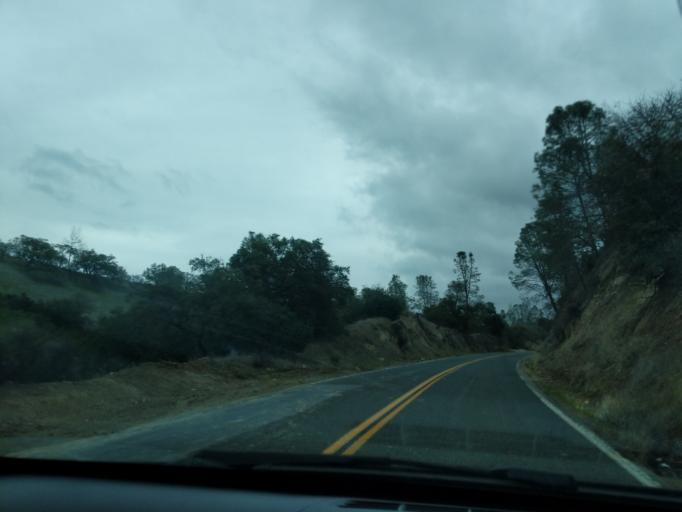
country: US
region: California
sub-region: Monterey County
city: Soledad
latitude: 36.5781
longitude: -121.1882
